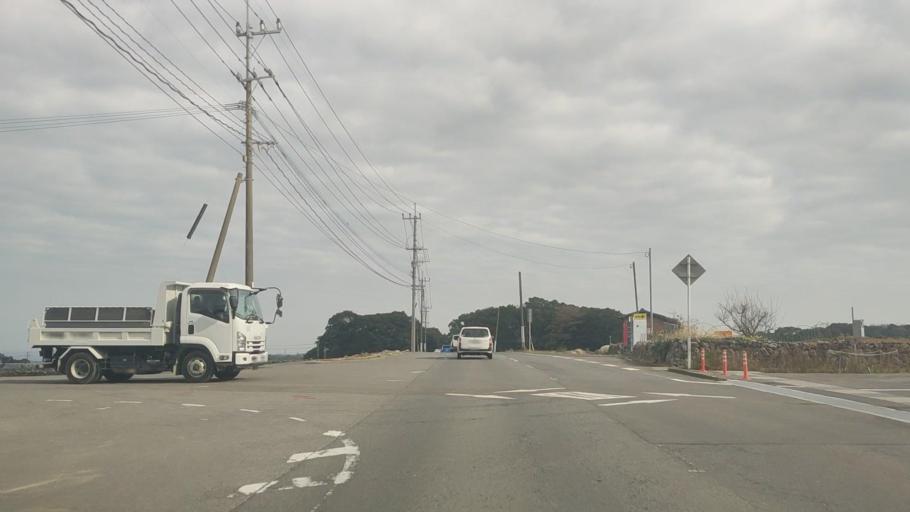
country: JP
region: Nagasaki
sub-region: Isahaya-shi
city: Isahaya
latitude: 32.8199
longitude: 130.1863
